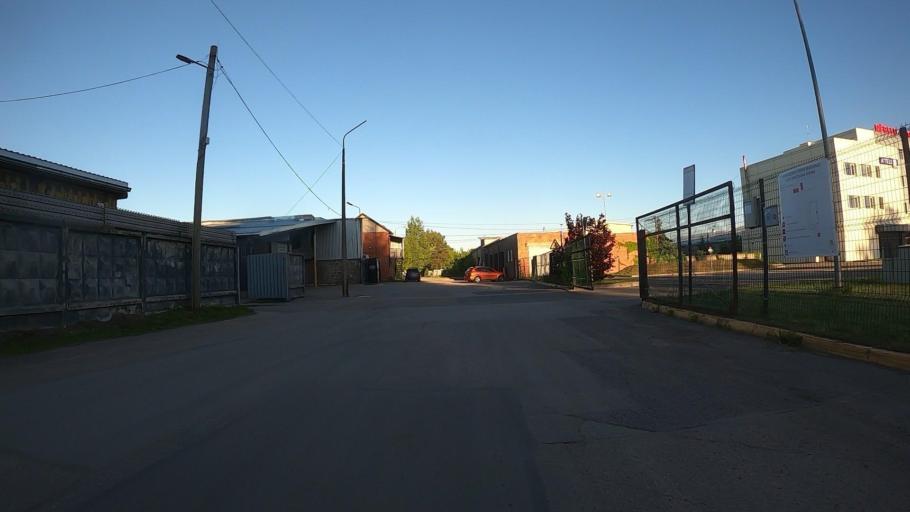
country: LV
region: Kekava
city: Kekava
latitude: 56.8805
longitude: 24.2453
